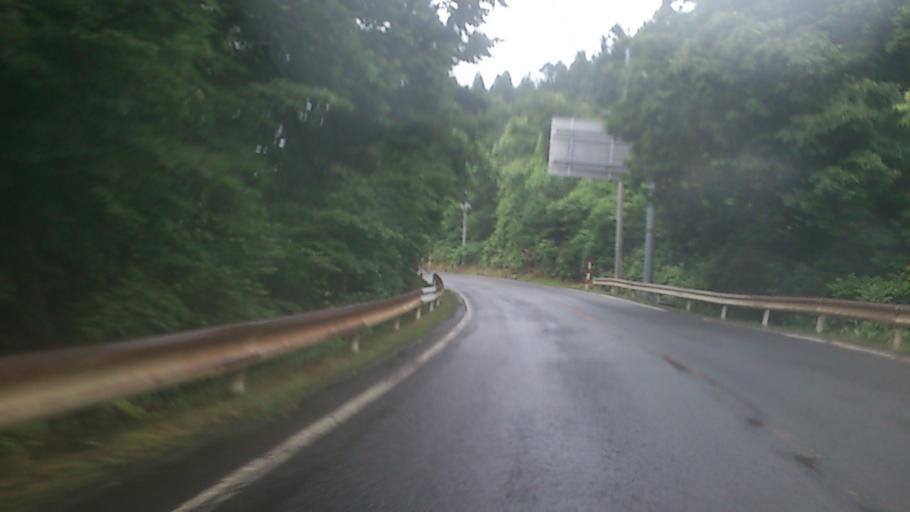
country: JP
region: Akita
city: Noshiromachi
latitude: 40.4221
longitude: 139.9481
